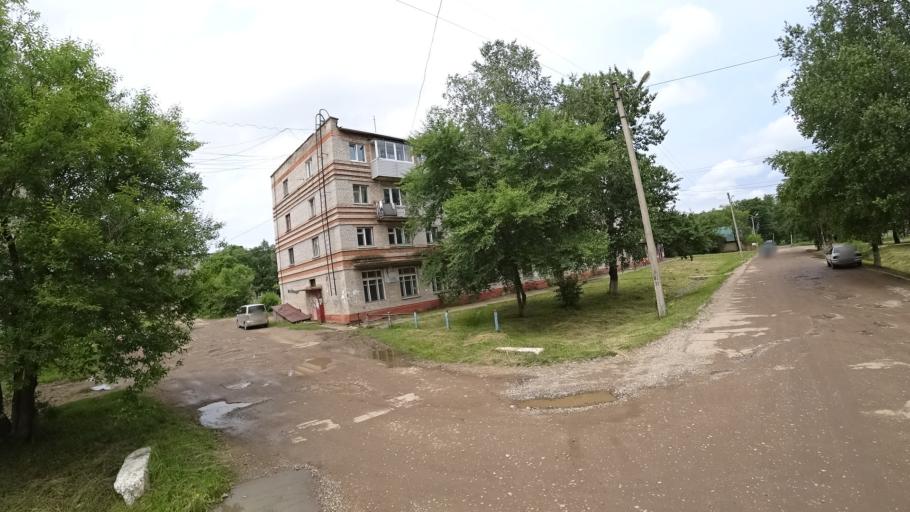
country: RU
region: Primorskiy
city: Novosysoyevka
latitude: 44.2281
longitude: 133.3611
